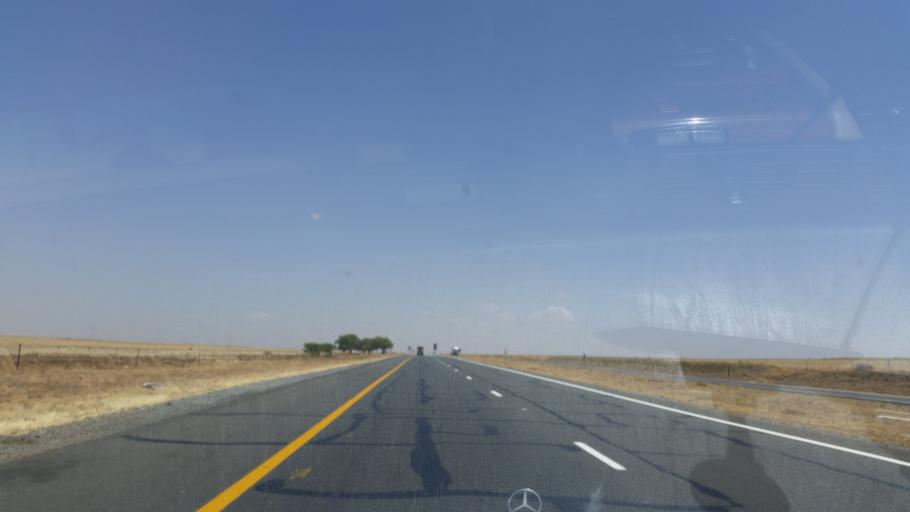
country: ZA
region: Orange Free State
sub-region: Lejweleputswa District Municipality
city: Brandfort
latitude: -28.8677
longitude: 26.5293
